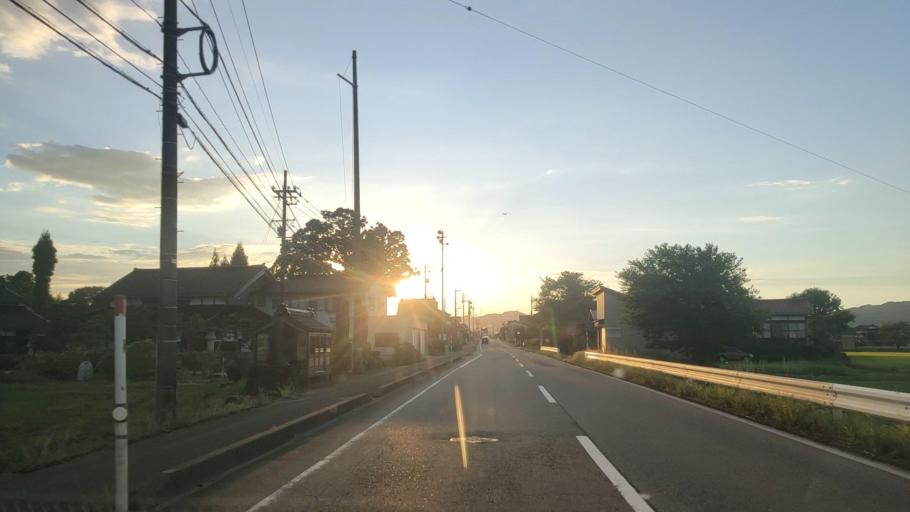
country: JP
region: Toyama
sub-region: Oyabe Shi
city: Oyabe
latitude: 36.6317
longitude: 136.8649
